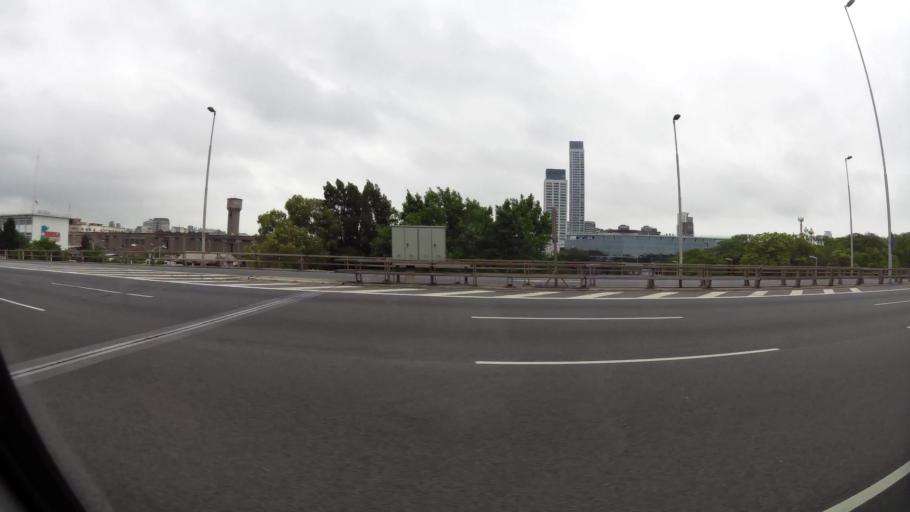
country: AR
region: Buenos Aires F.D.
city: Retiro
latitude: -34.5718
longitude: -58.4007
